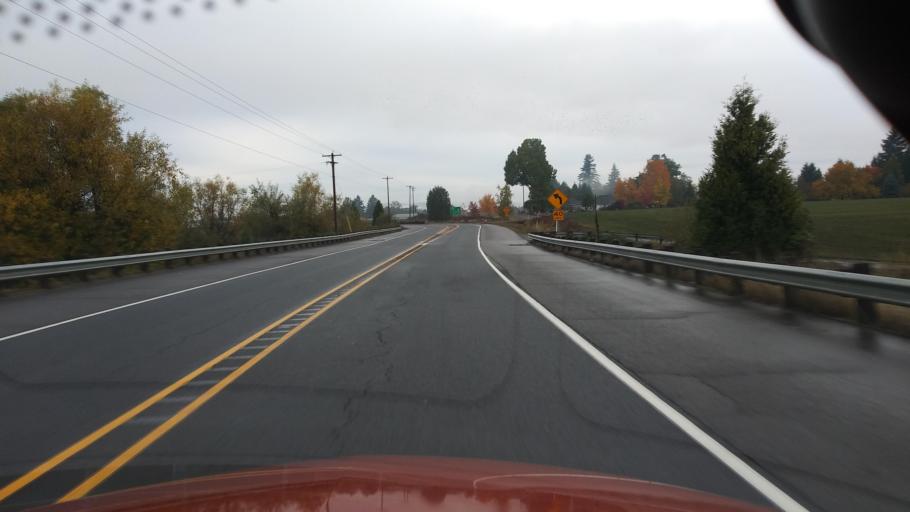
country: US
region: Oregon
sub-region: Washington County
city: Cornelius
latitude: 45.5490
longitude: -123.0615
